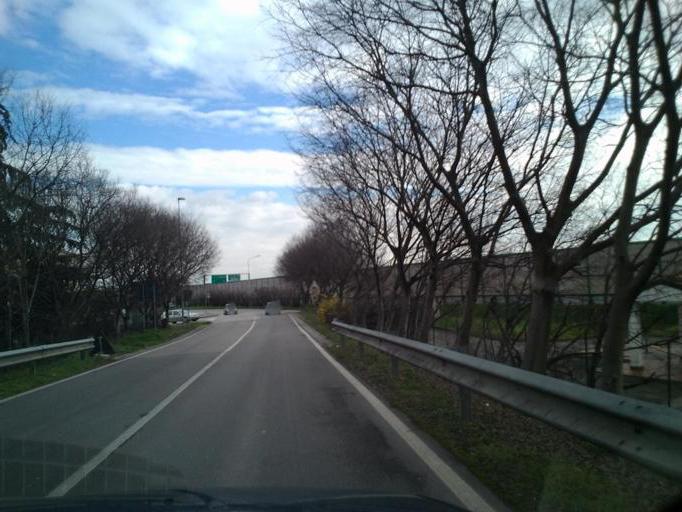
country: IT
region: Veneto
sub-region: Provincia di Verona
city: Caselle
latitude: 45.4132
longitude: 10.8970
